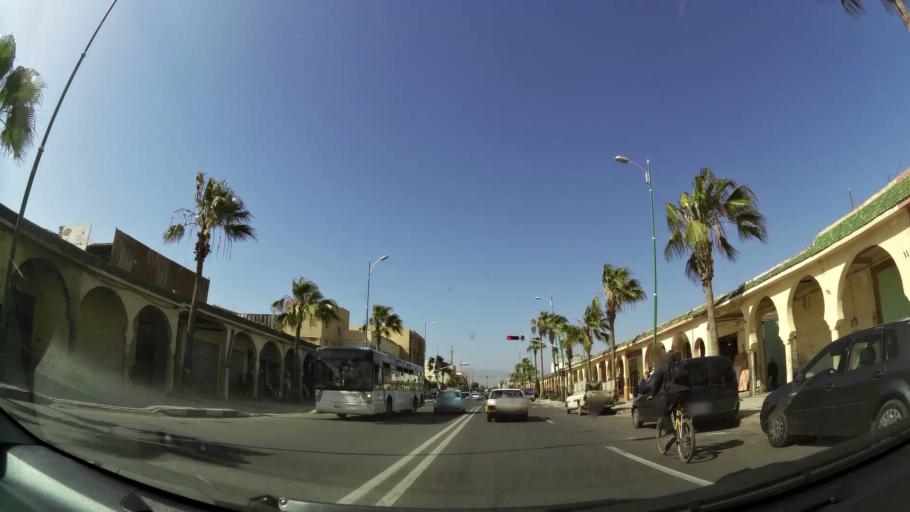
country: MA
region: Souss-Massa-Draa
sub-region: Inezgane-Ait Mellou
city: Inezgane
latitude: 30.3651
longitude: -9.5332
